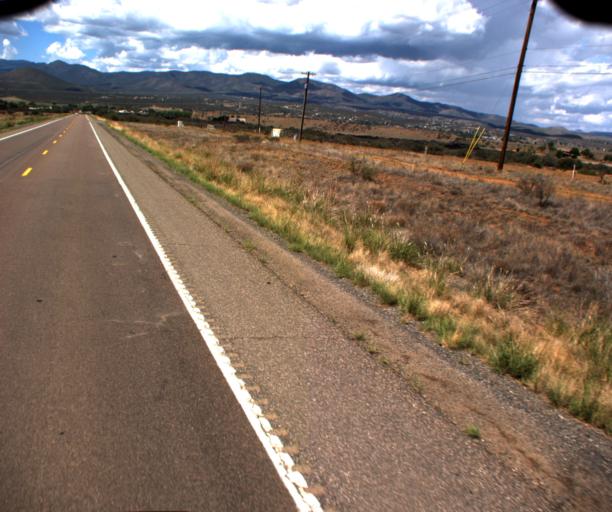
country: US
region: Arizona
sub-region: Yavapai County
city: Dewey-Humboldt
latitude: 34.5366
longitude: -112.2098
